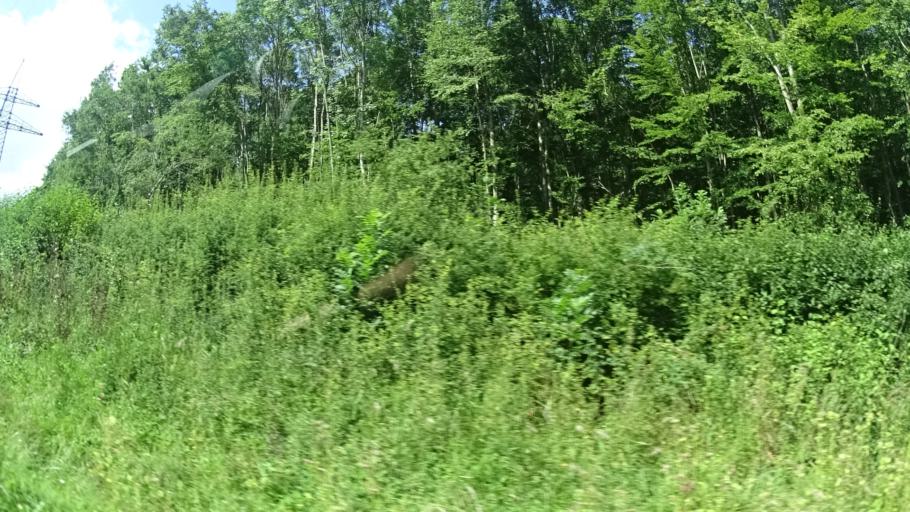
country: DE
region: Bavaria
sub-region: Regierungsbezirk Unterfranken
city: Rentweinsdorf
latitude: 50.0883
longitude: 10.8351
